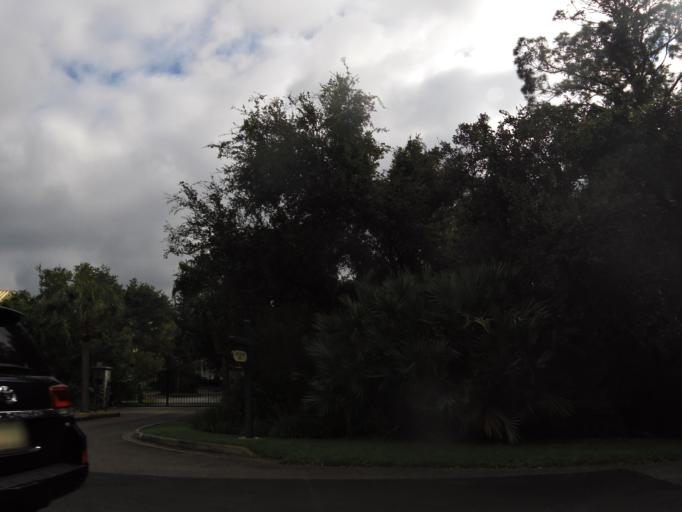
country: US
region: Georgia
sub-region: Glynn County
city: Saint Simons Island
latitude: 31.1479
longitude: -81.3803
